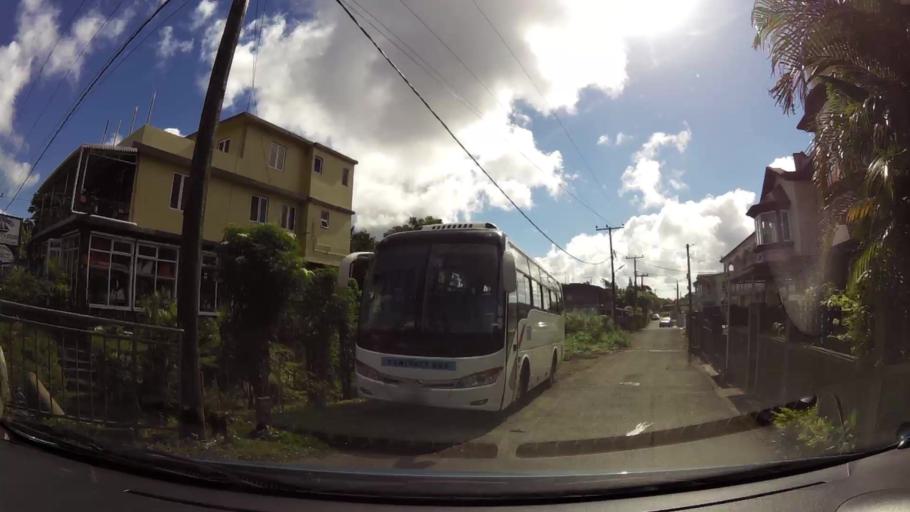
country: MU
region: Plaines Wilhems
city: Curepipe
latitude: -20.3322
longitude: 57.5209
